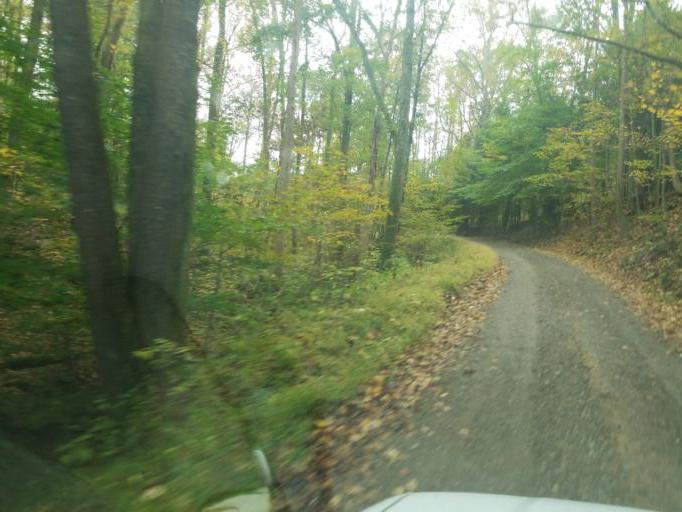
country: US
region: Ohio
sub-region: Holmes County
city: Millersburg
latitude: 40.5454
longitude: -82.0388
